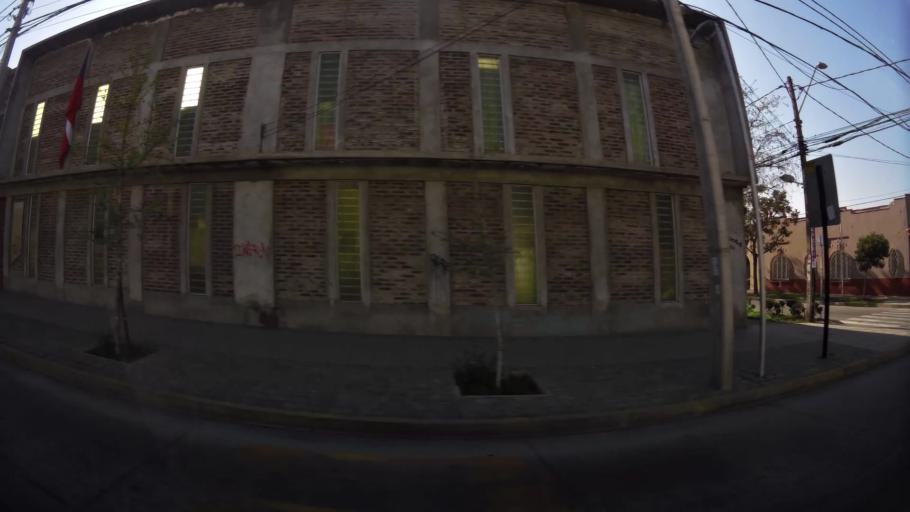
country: CL
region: Santiago Metropolitan
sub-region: Provincia de Santiago
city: Santiago
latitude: -33.4598
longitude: -70.6363
